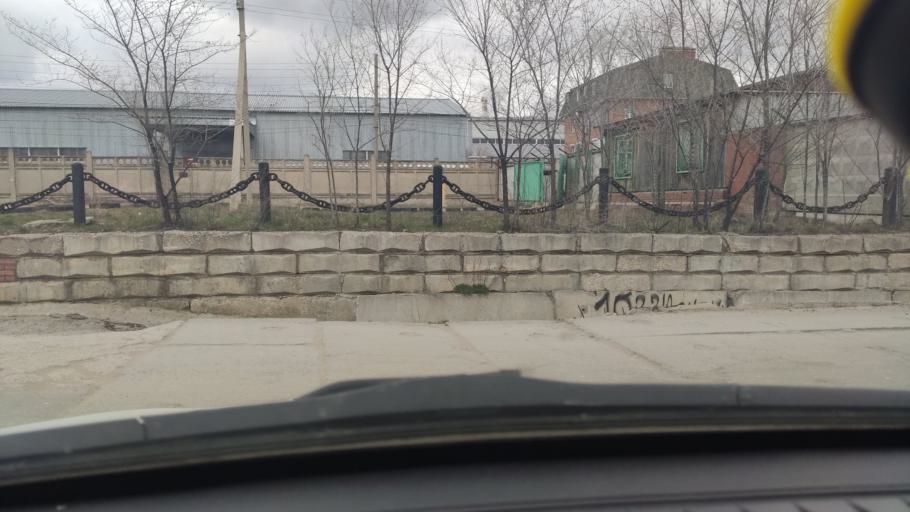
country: RU
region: Samara
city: Zhigulevsk
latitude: 53.4811
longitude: 49.4906
